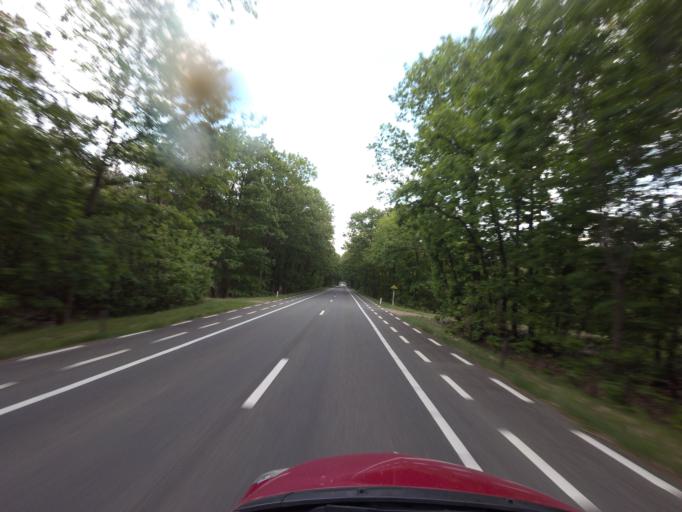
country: BE
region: Flanders
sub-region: Provincie Limburg
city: Overpelt
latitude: 51.1703
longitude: 5.3642
